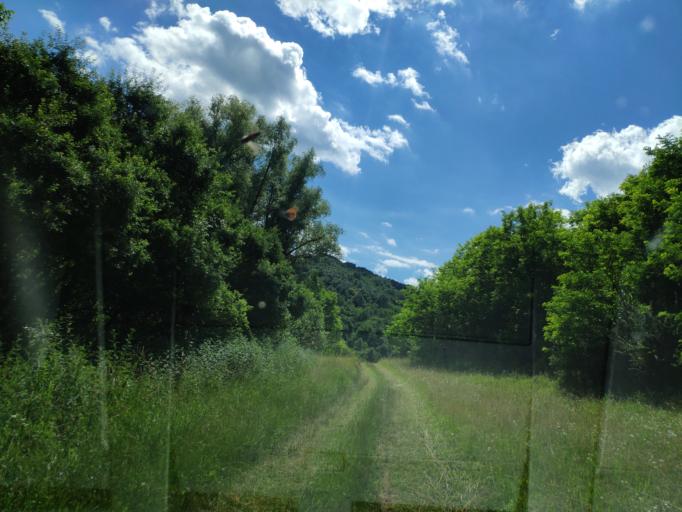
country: HU
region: Borsod-Abauj-Zemplen
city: Arlo
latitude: 48.2560
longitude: 20.1805
